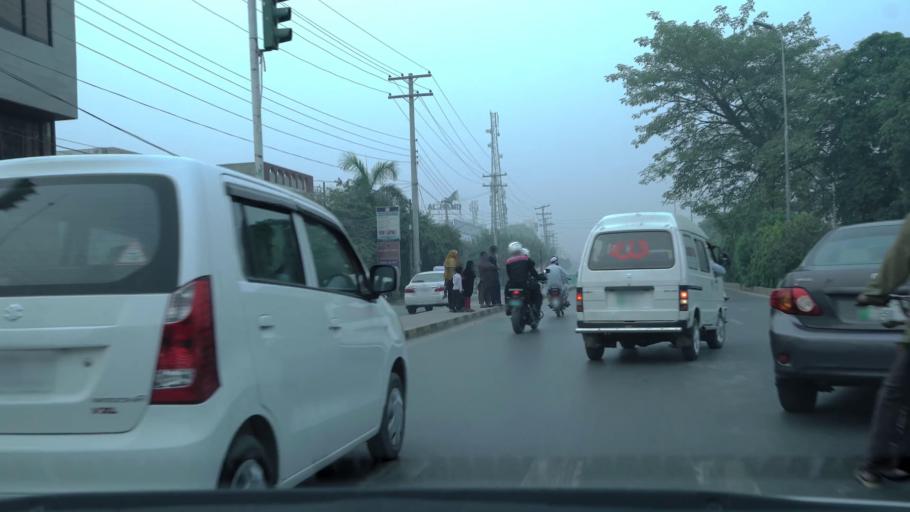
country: PK
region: Punjab
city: Lahore
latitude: 31.4745
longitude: 74.3021
